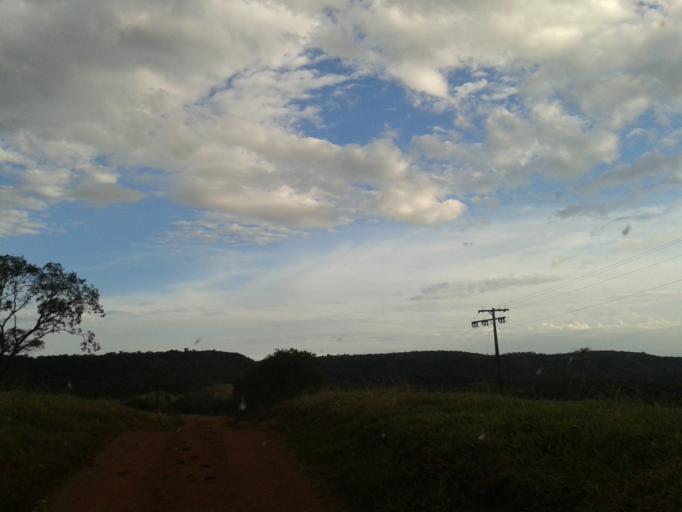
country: BR
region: Minas Gerais
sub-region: Campina Verde
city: Campina Verde
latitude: -19.3487
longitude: -49.6674
